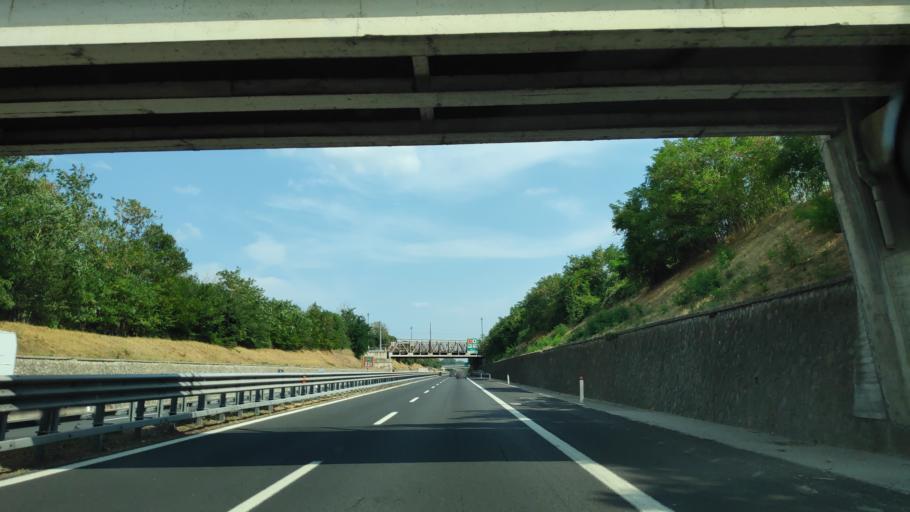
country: IT
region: Umbria
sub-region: Provincia di Terni
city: Attigliano
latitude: 42.5048
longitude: 12.3025
